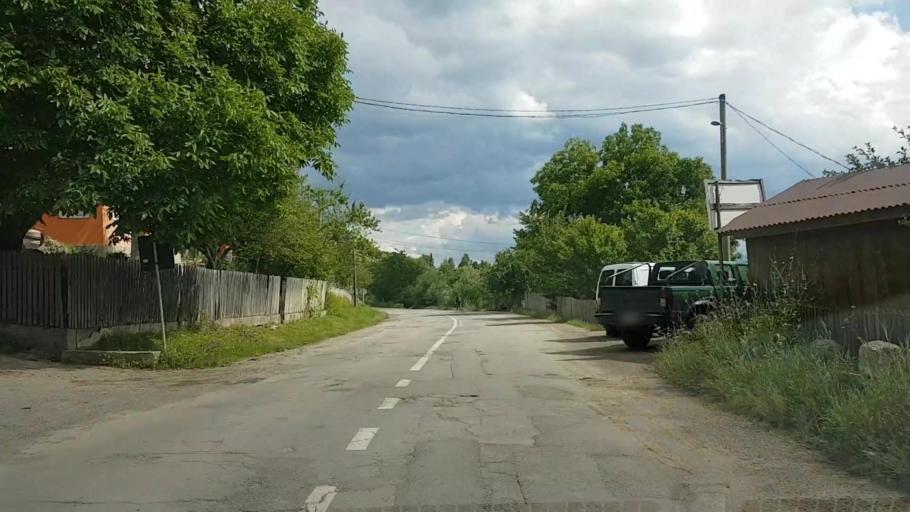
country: RO
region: Neamt
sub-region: Comuna Hangu
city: Hangu
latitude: 47.0437
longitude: 26.0542
